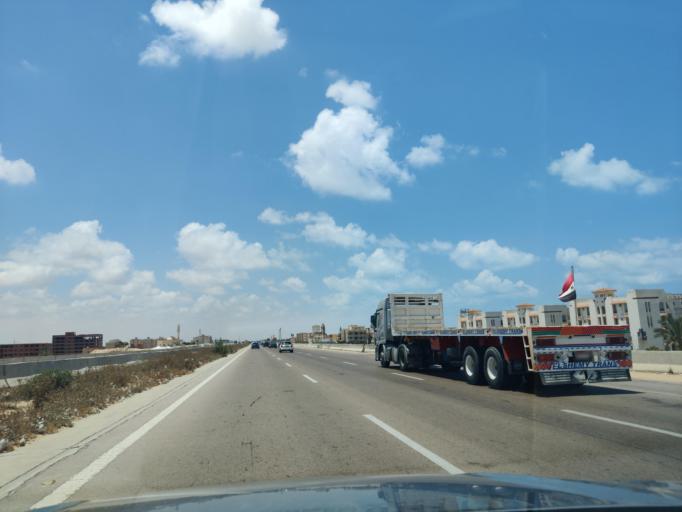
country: EG
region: Muhafazat Matruh
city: Al `Alamayn
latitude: 30.8367
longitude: 29.2402
